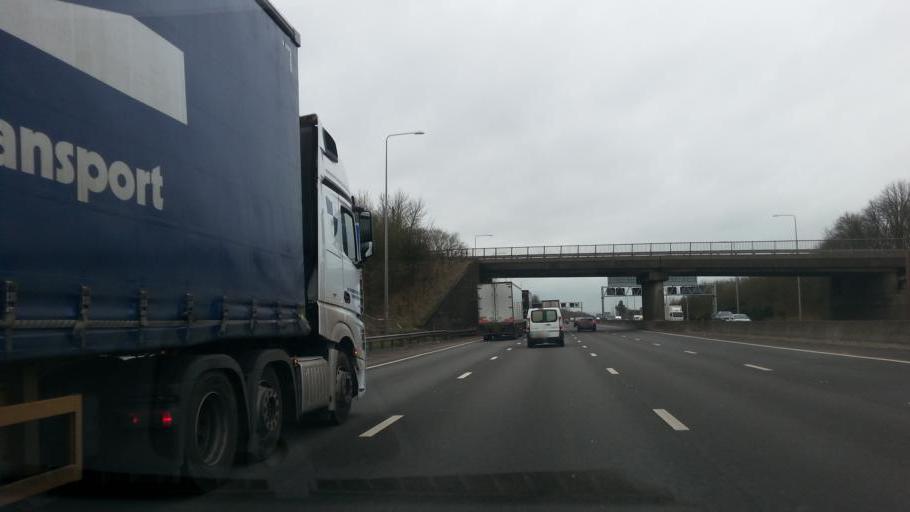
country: GB
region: England
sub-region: Derbyshire
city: Pinxton
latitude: 53.0722
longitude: -1.2821
